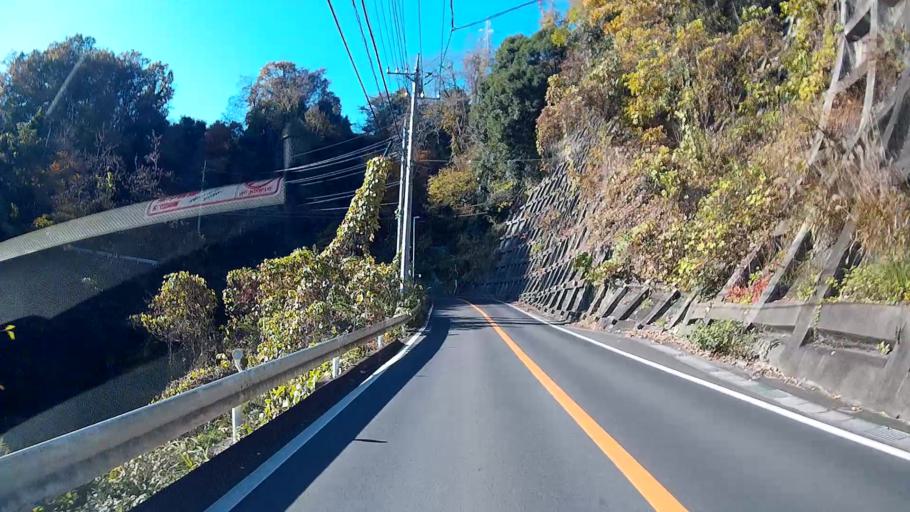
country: JP
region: Yamanashi
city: Uenohara
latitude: 35.6078
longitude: 139.1237
